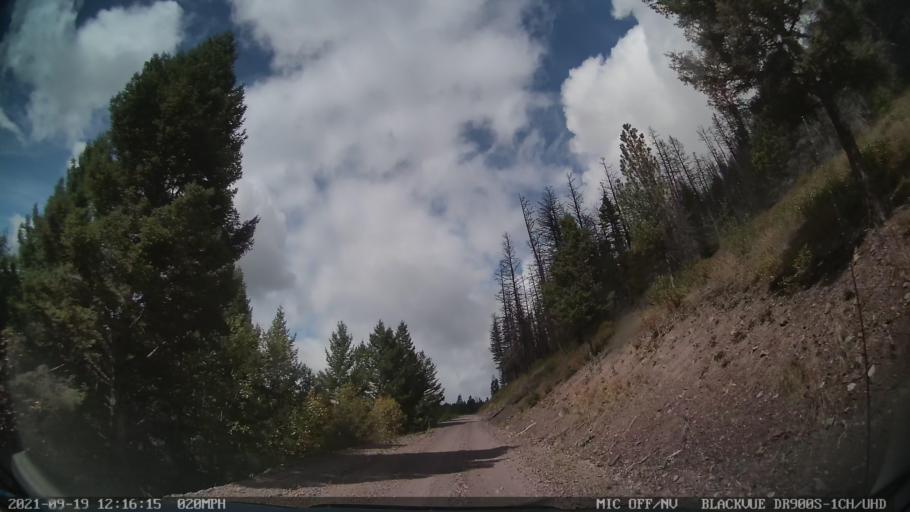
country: US
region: Montana
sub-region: Missoula County
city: Seeley Lake
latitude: 47.1690
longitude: -113.3499
